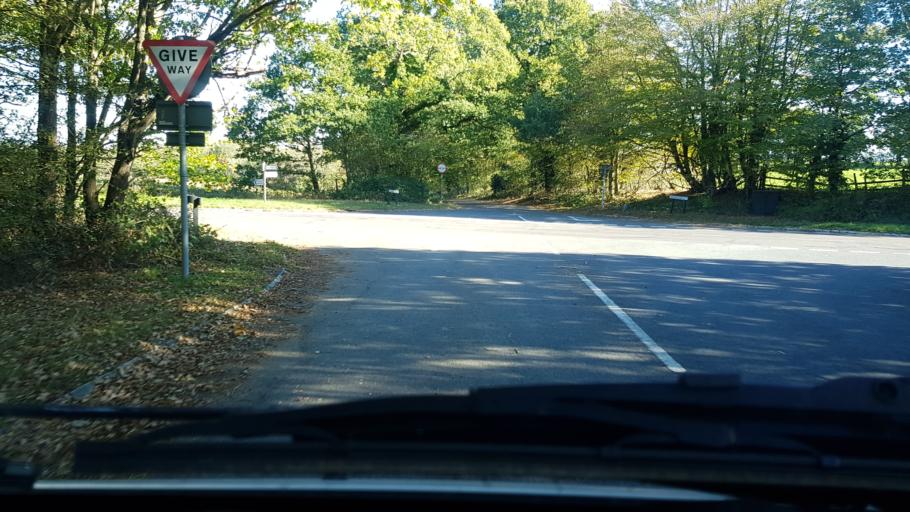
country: GB
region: England
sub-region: Surrey
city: Ockley
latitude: 51.1238
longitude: -0.3707
